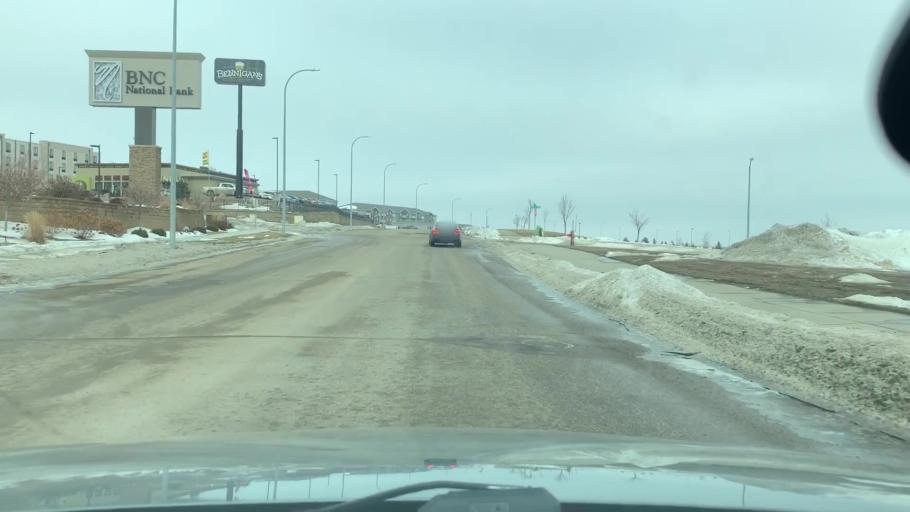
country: US
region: North Dakota
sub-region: Morton County
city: Mandan
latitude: 46.8496
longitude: -100.9093
